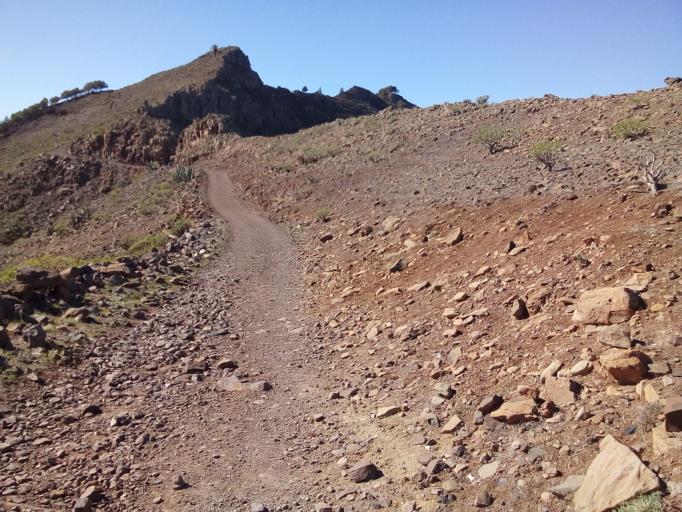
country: ES
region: Canary Islands
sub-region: Provincia de Santa Cruz de Tenerife
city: Vallehermosa
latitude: 28.1227
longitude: -17.3293
